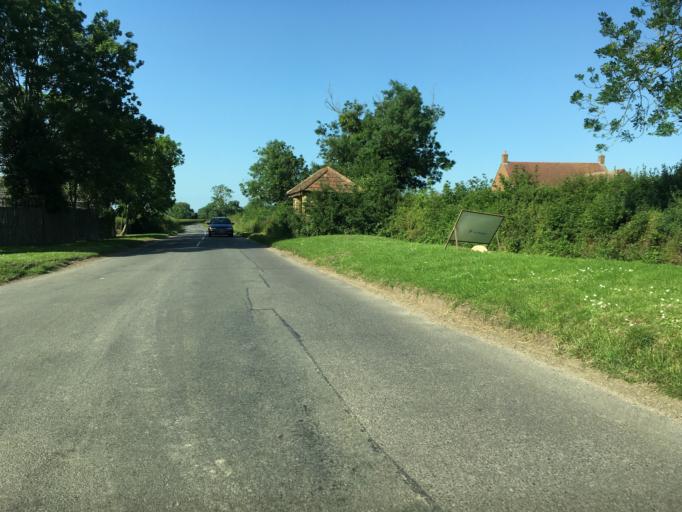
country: GB
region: England
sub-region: Buckinghamshire
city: Steeple Claydon
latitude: 51.9243
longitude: -1.0557
